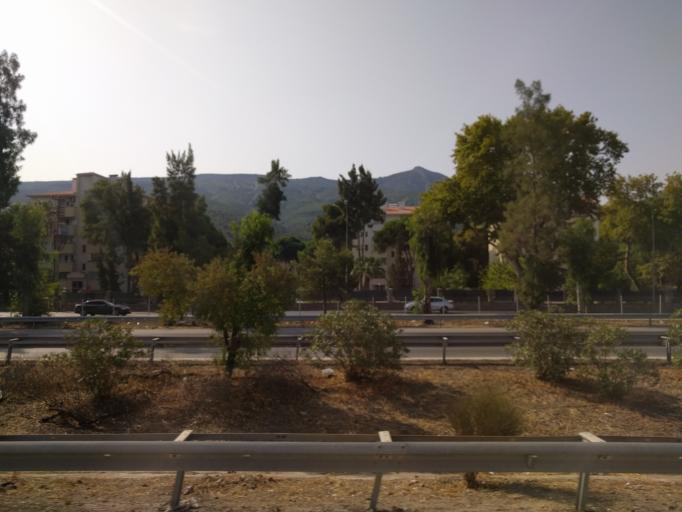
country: TR
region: Izmir
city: Karsiyaka
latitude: 38.3940
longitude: 26.9678
